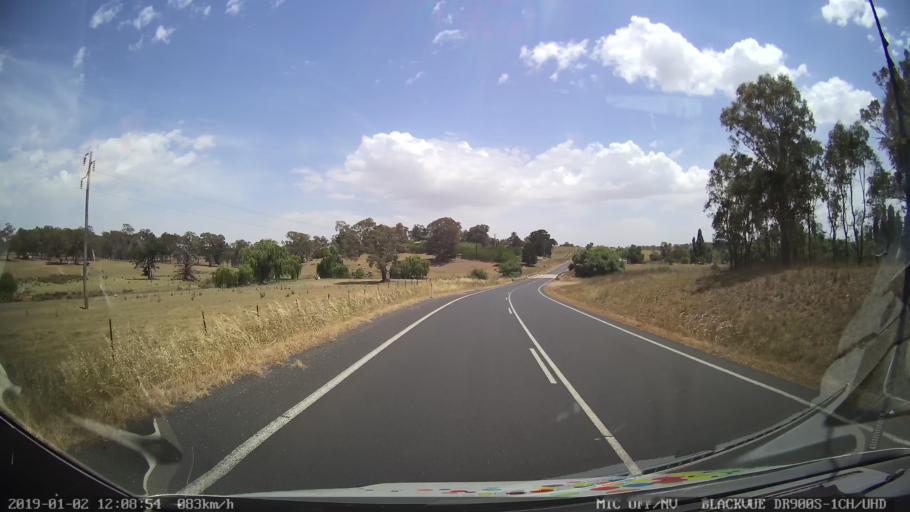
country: AU
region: New South Wales
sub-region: Young
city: Young
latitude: -34.4785
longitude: 148.2728
